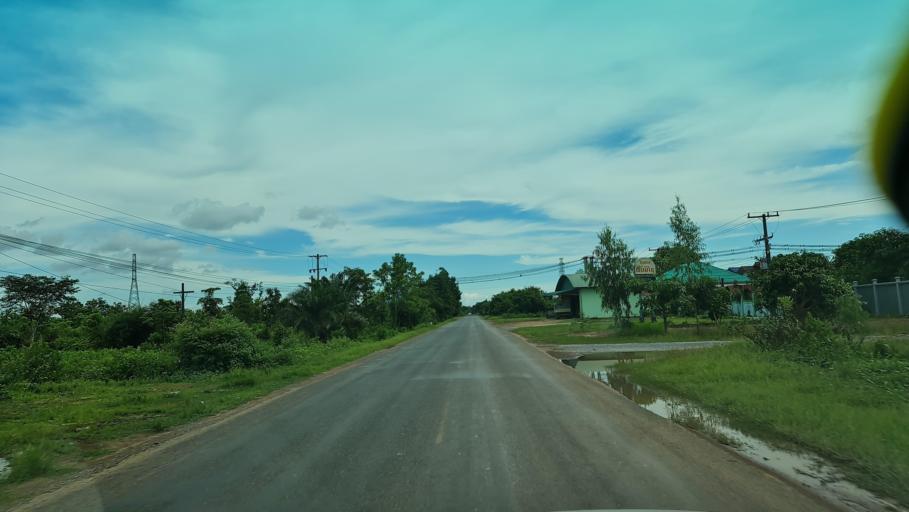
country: TH
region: Nakhon Phanom
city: Ban Phaeng
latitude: 18.0858
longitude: 104.2904
